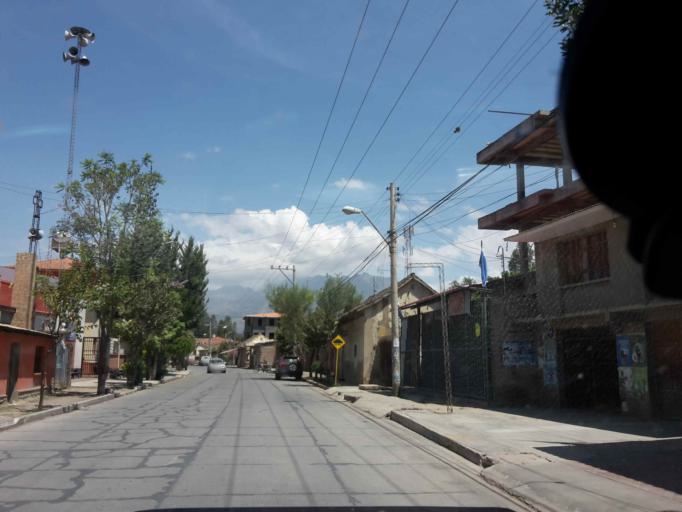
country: BO
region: Cochabamba
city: Cochabamba
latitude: -17.3611
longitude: -66.2274
